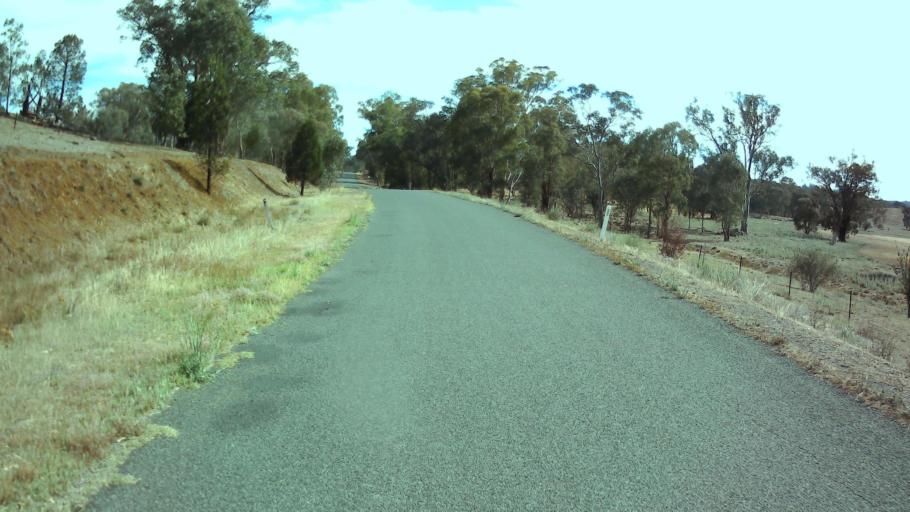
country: AU
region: New South Wales
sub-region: Weddin
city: Grenfell
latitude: -33.8173
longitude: 148.2915
